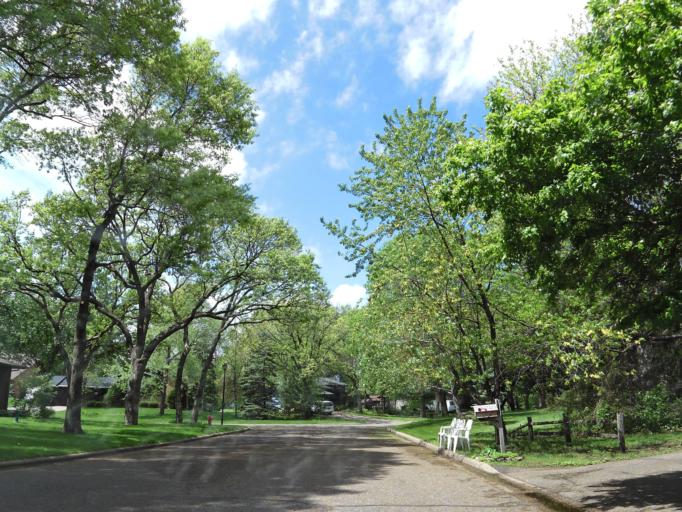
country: US
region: Wisconsin
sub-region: Saint Croix County
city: Hudson
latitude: 44.9837
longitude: -92.7327
